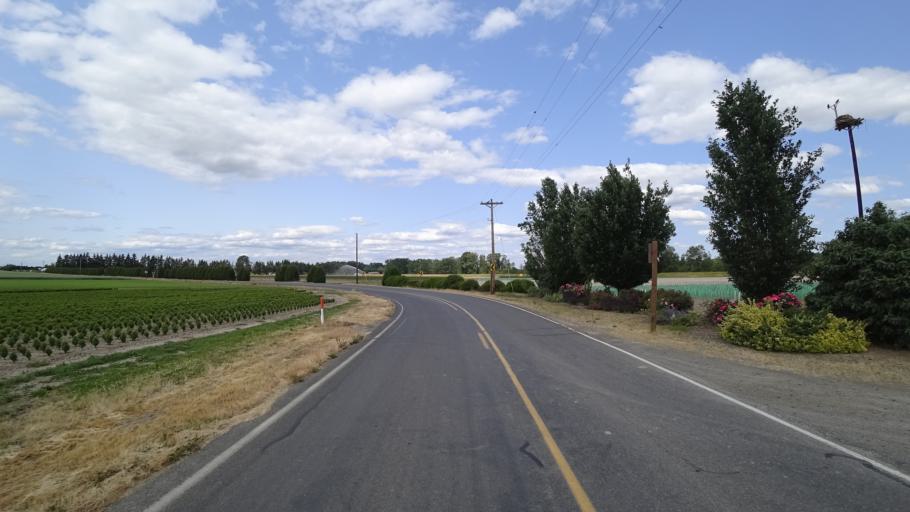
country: US
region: Washington
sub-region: Clark County
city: Felida
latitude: 45.6471
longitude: -122.7772
